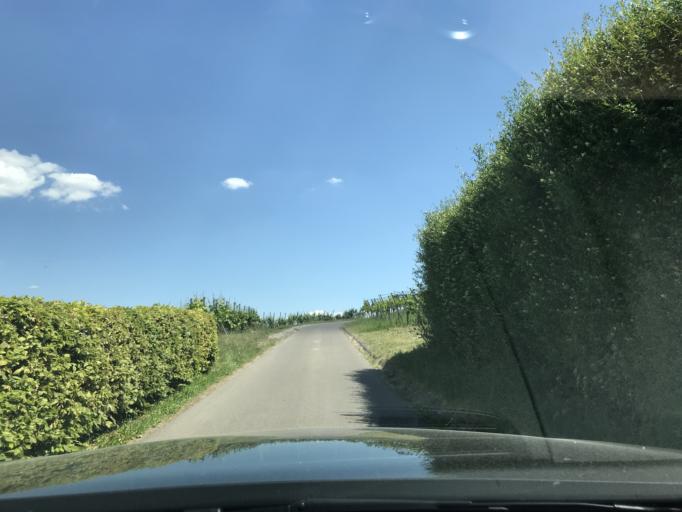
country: DE
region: Baden-Wuerttemberg
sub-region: Regierungsbezirk Stuttgart
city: Weinstadt-Endersbach
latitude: 48.7949
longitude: 9.3818
